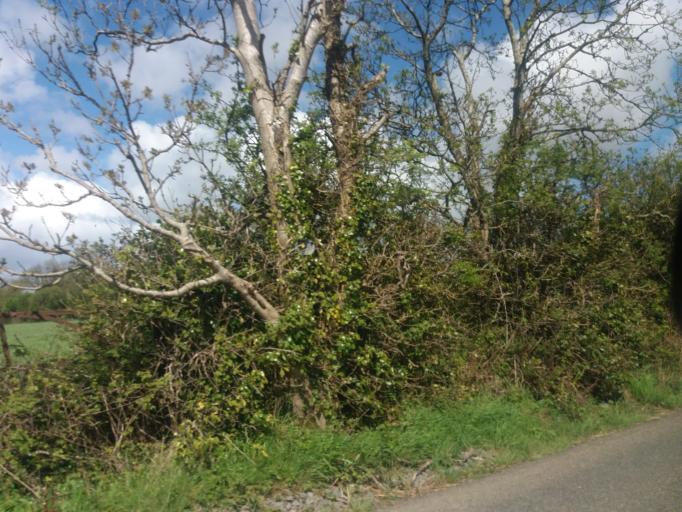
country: IE
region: Munster
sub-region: Waterford
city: Dunmore East
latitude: 52.2376
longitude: -6.8555
